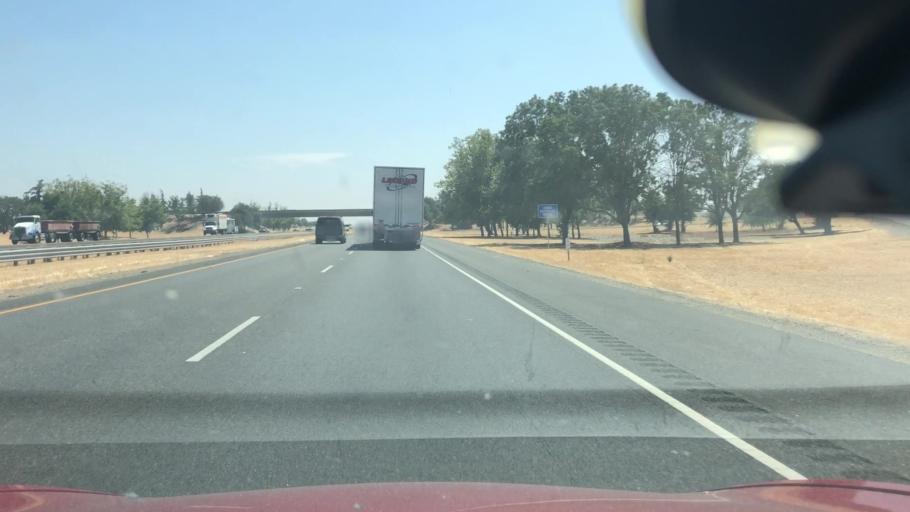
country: US
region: California
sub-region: Sacramento County
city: Laguna
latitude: 38.4115
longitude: -121.4846
